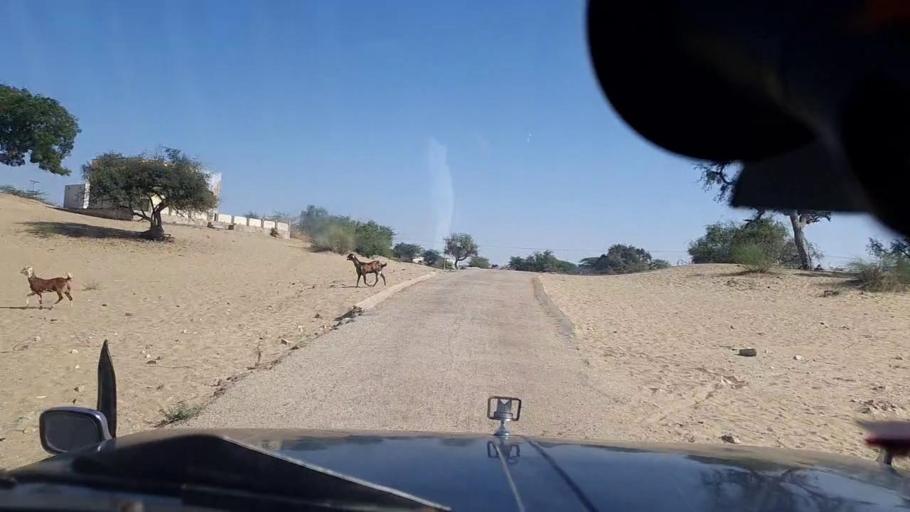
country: PK
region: Sindh
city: Diplo
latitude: 24.4522
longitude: 69.6965
